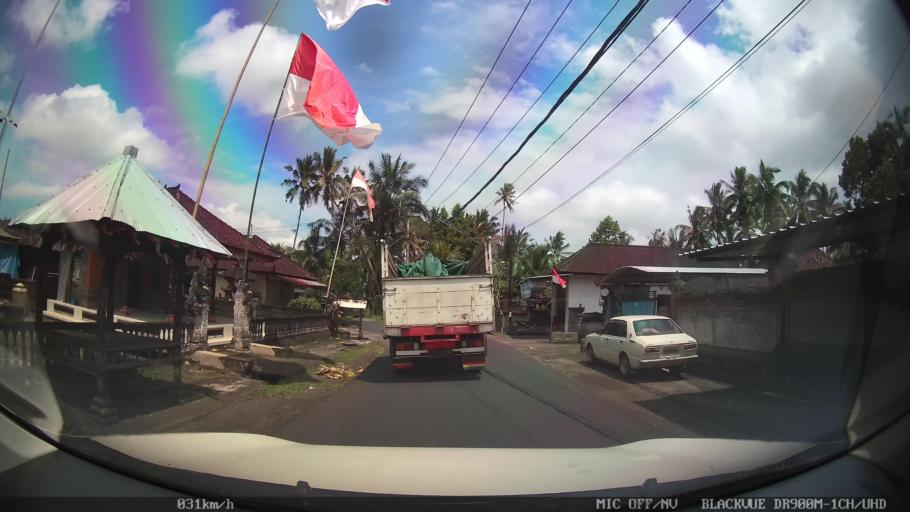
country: ID
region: Bali
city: Banjar Kelodan
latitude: -8.4851
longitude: 115.3673
